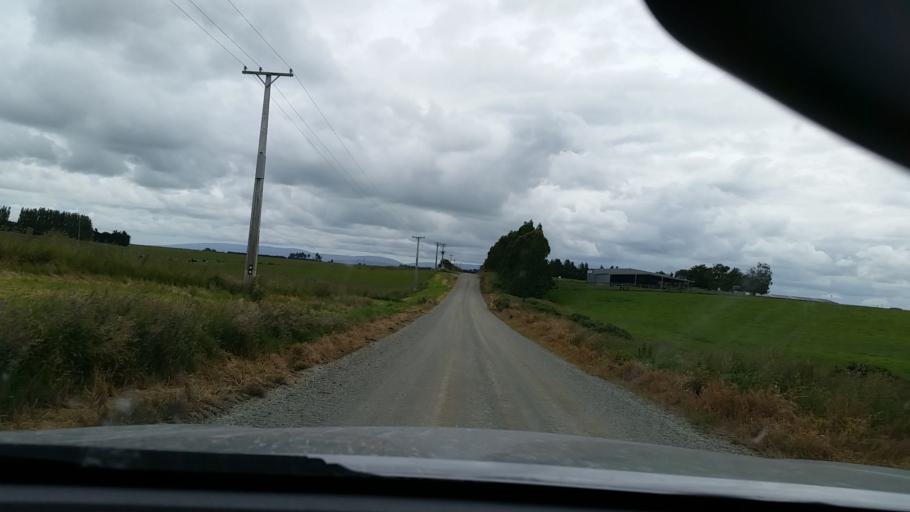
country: NZ
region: Southland
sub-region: Southland District
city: Winton
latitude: -46.1854
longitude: 168.2221
